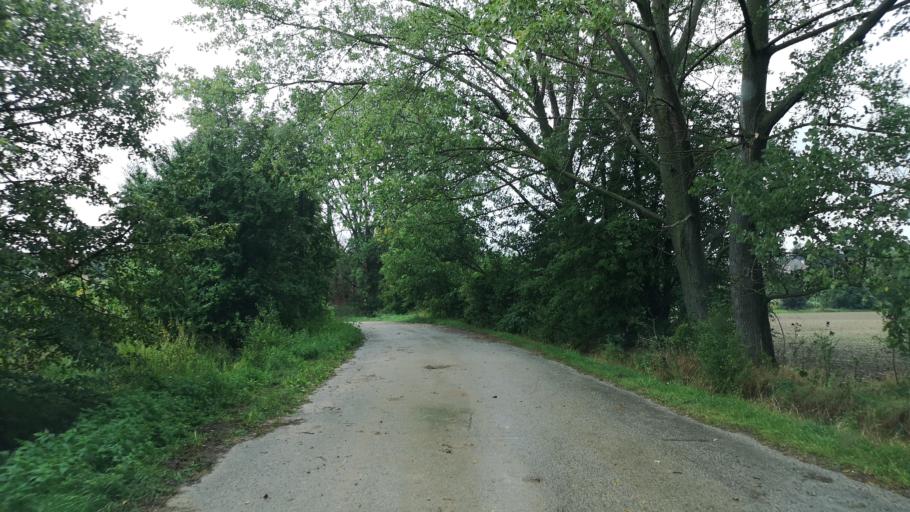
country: SK
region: Trnavsky
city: Smolenice
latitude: 48.5213
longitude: 17.5240
